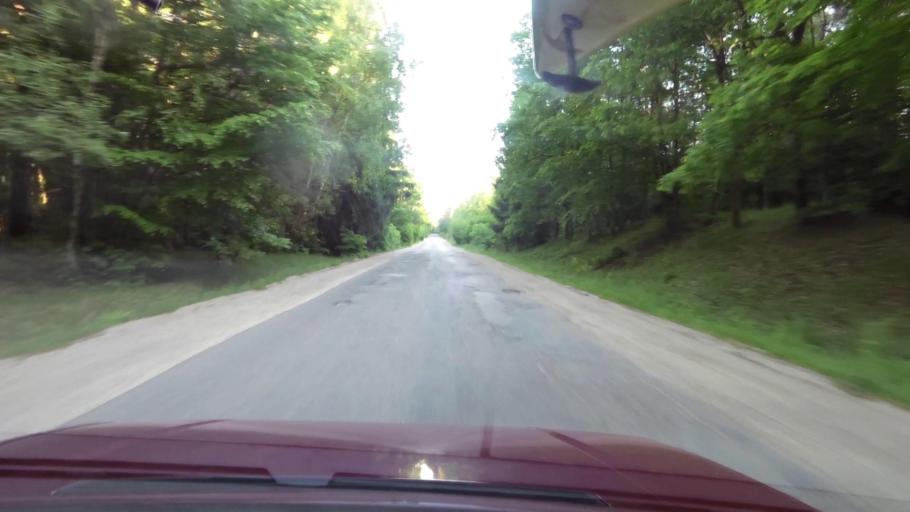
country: PL
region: West Pomeranian Voivodeship
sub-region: Powiat szczecinecki
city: Bialy Bor
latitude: 53.9302
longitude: 16.8002
